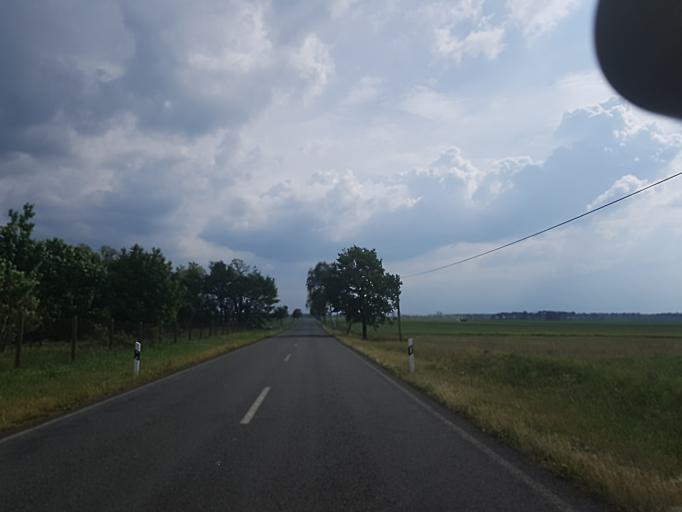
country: DE
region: Saxony-Anhalt
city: Rodleben
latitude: 52.0048
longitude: 12.2337
